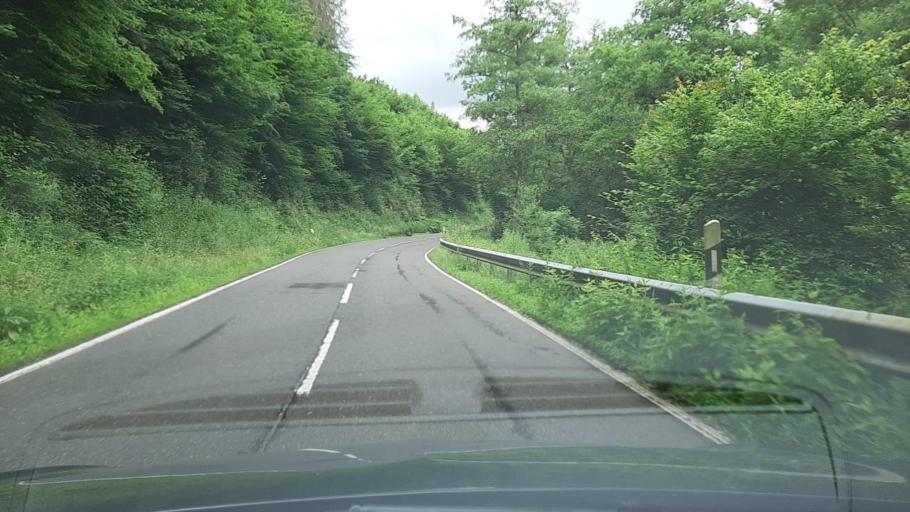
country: DE
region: Rheinland-Pfalz
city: Macken
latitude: 50.1920
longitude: 7.4139
